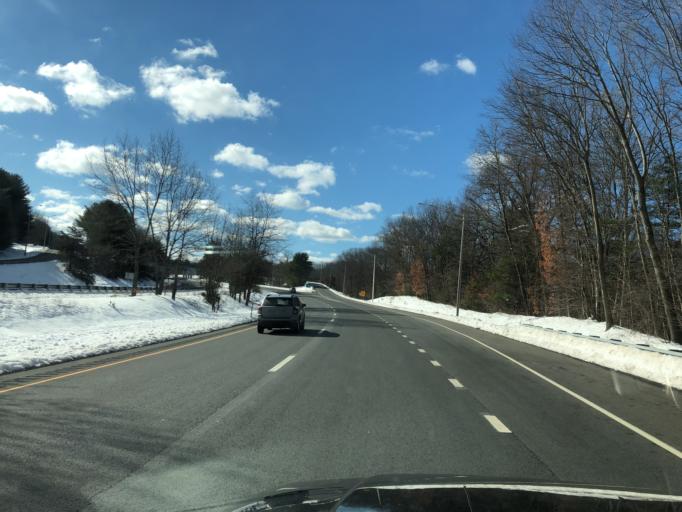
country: US
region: Connecticut
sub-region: Hartford County
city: Glastonbury Center
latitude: 41.6807
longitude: -72.5417
